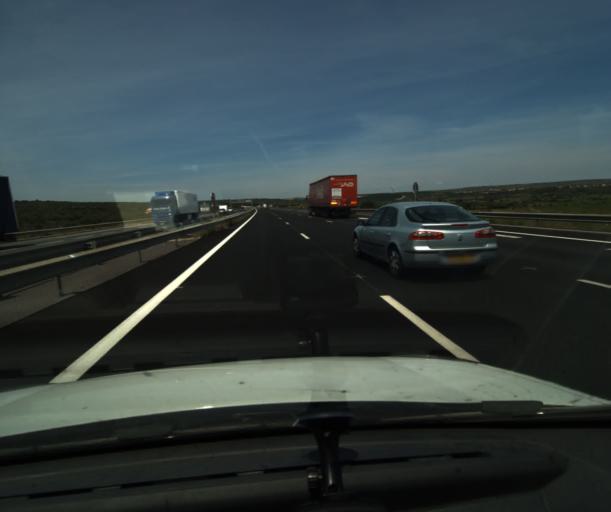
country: FR
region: Languedoc-Roussillon
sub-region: Departement de l'Aude
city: Sigean
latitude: 42.9552
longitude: 2.9705
